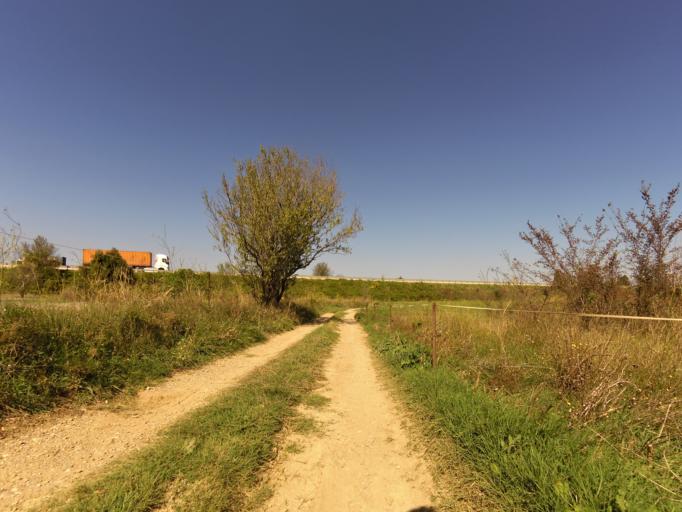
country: FR
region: Languedoc-Roussillon
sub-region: Departement du Gard
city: Gallargues-le-Montueux
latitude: 43.7232
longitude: 4.1551
